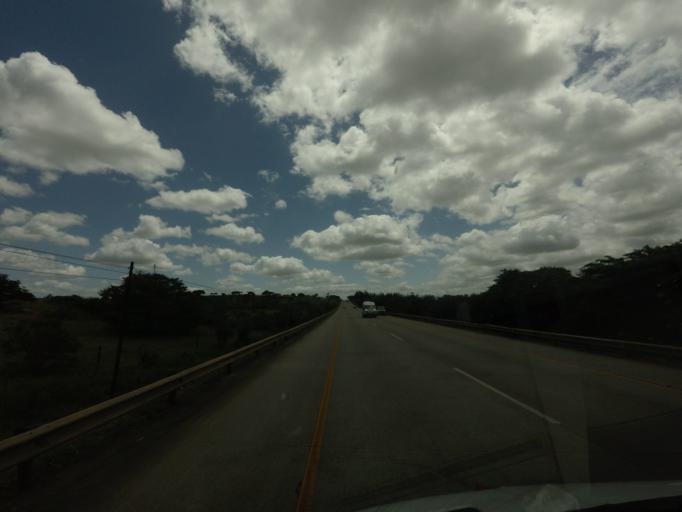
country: ZA
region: KwaZulu-Natal
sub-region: uMkhanyakude District Municipality
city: Mtubatuba
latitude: -28.4825
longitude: 32.1430
